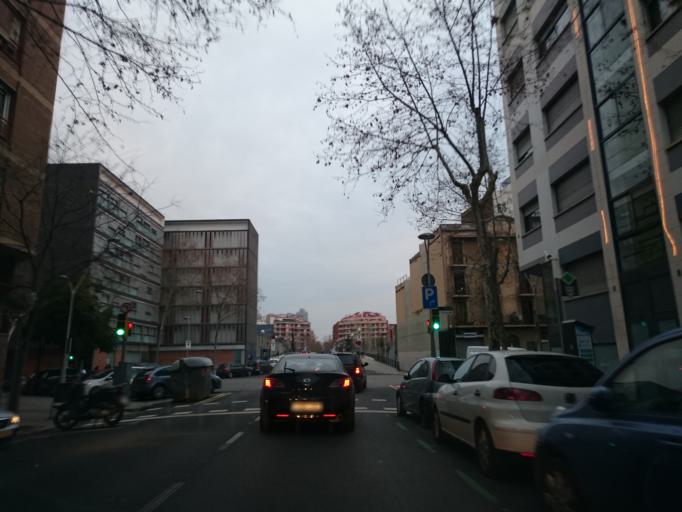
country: ES
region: Catalonia
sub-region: Provincia de Barcelona
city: Ciutat Vella
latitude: 41.3959
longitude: 2.1833
